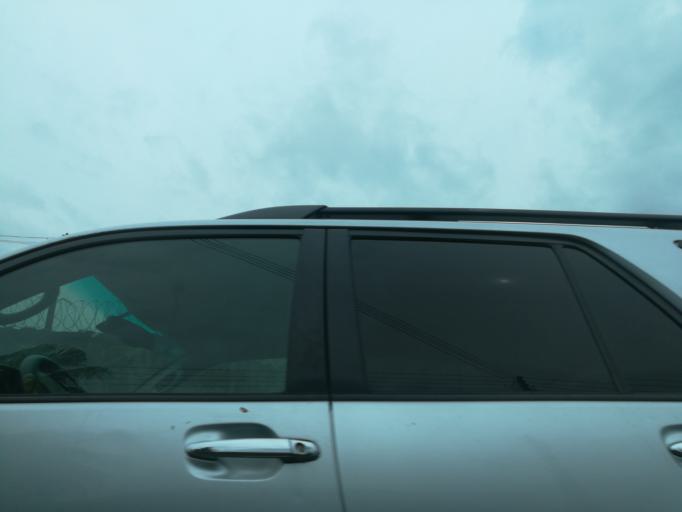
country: NG
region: Rivers
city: Port Harcourt
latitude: 4.8338
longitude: 7.0278
